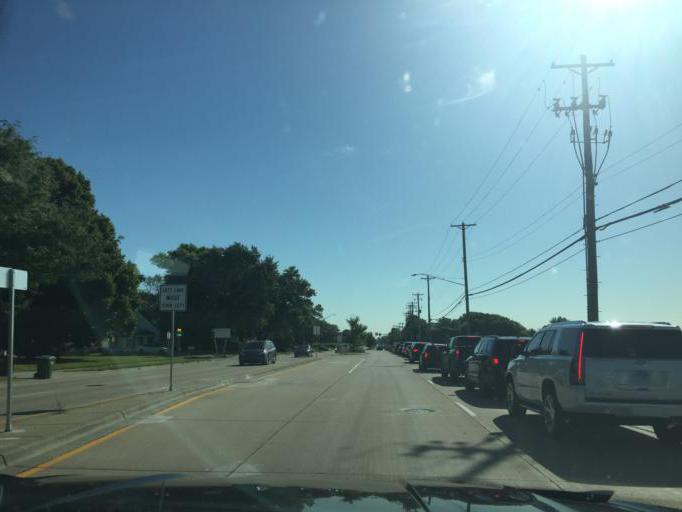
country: US
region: Minnesota
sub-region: Ramsey County
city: Falcon Heights
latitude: 44.9917
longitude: -93.1798
